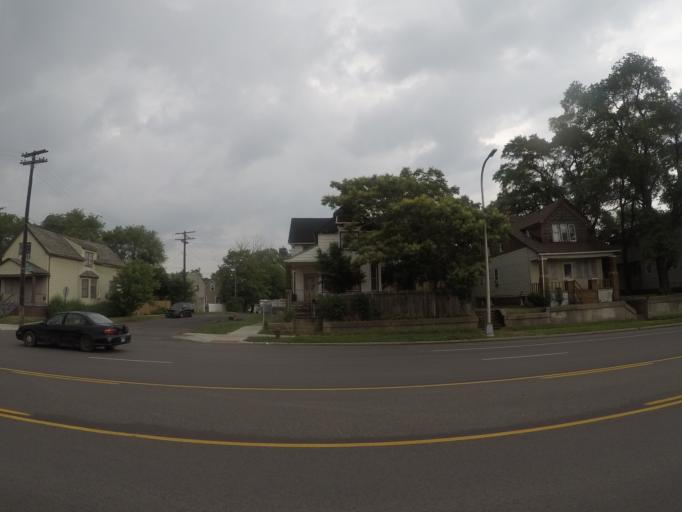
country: US
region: Michigan
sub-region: Wayne County
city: River Rouge
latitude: 42.3196
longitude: -83.1120
